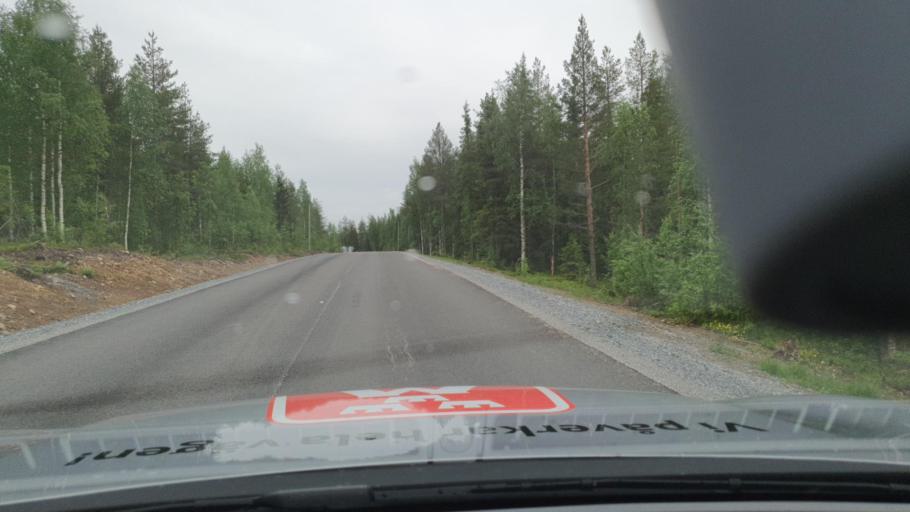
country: SE
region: Norrbotten
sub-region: Overtornea Kommun
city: OEvertornea
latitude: 66.5991
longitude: 23.3066
